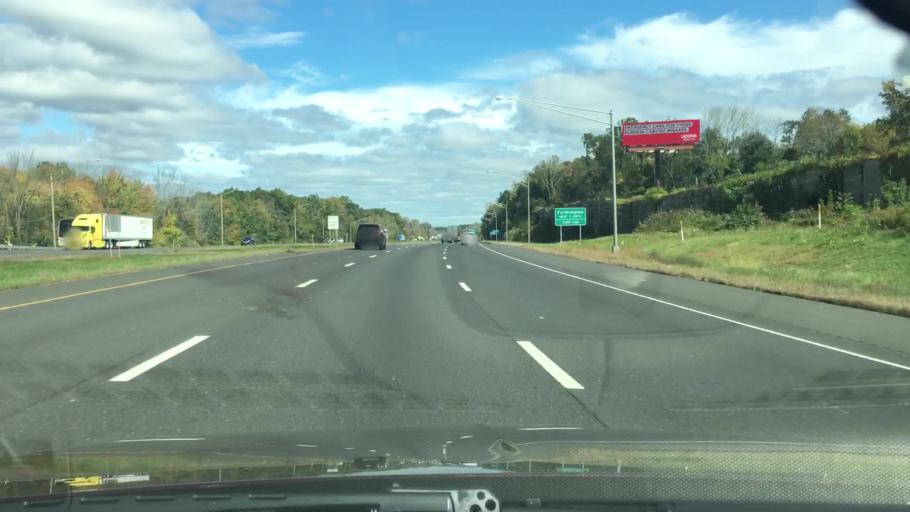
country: US
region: Connecticut
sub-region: Hartford County
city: Farmington
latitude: 41.6881
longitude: -72.8148
